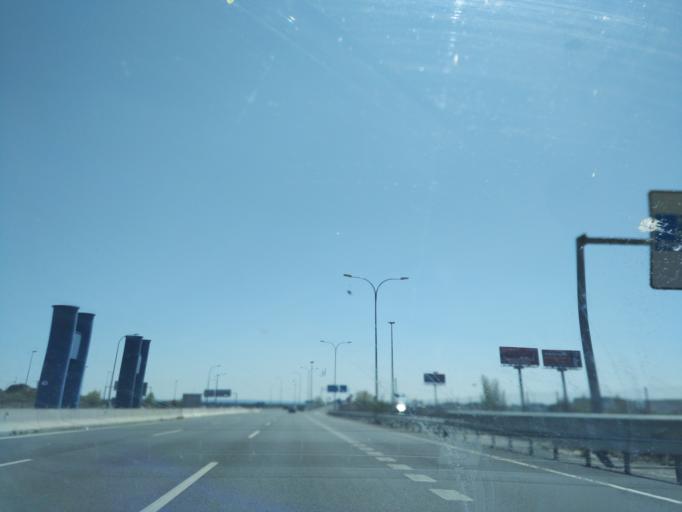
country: ES
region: Madrid
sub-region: Provincia de Madrid
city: Villa de Vallecas
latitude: 40.3631
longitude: -3.5726
